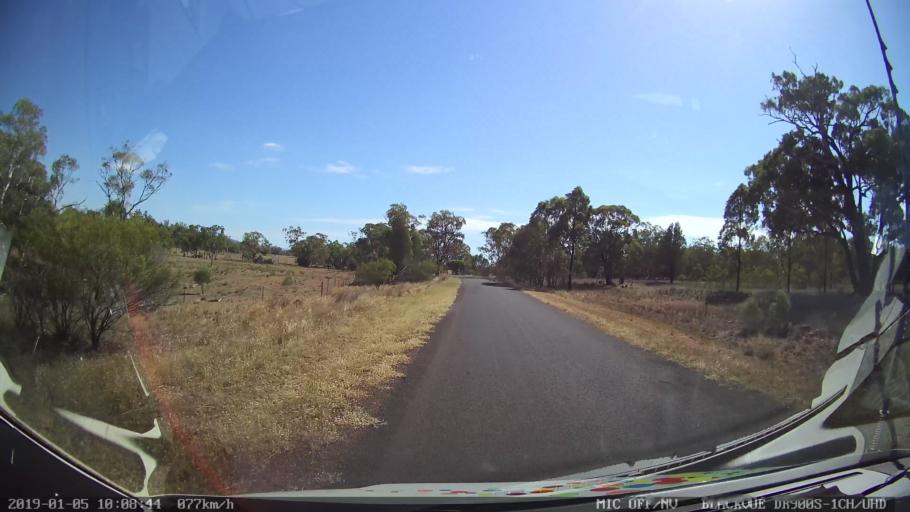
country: AU
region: New South Wales
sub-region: Gilgandra
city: Gilgandra
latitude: -31.6381
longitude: 148.8816
